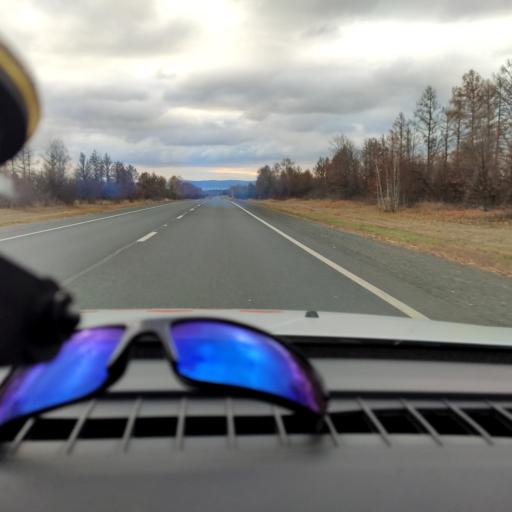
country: RU
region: Samara
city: Volzhskiy
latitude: 53.4740
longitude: 50.1194
